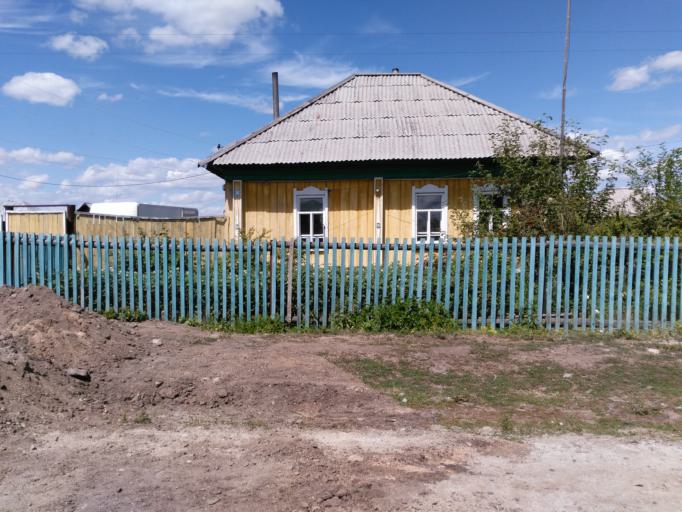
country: RU
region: Bashkortostan
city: Akhunovo
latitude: 54.2028
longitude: 59.5958
